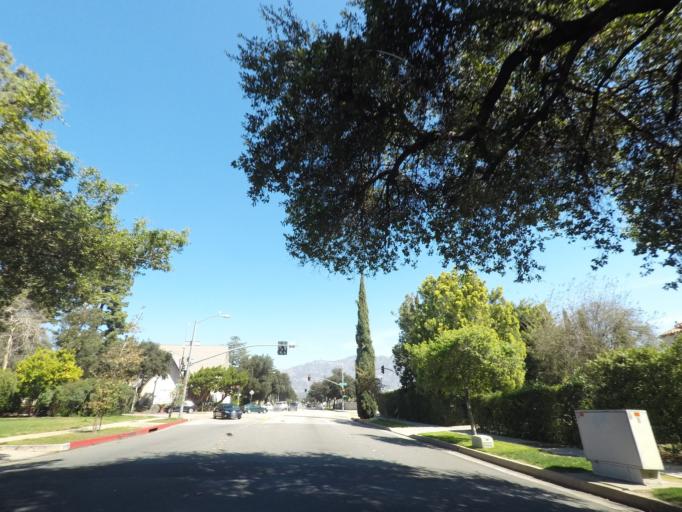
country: US
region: California
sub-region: Los Angeles County
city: Pasadena
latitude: 34.1413
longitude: -118.1213
